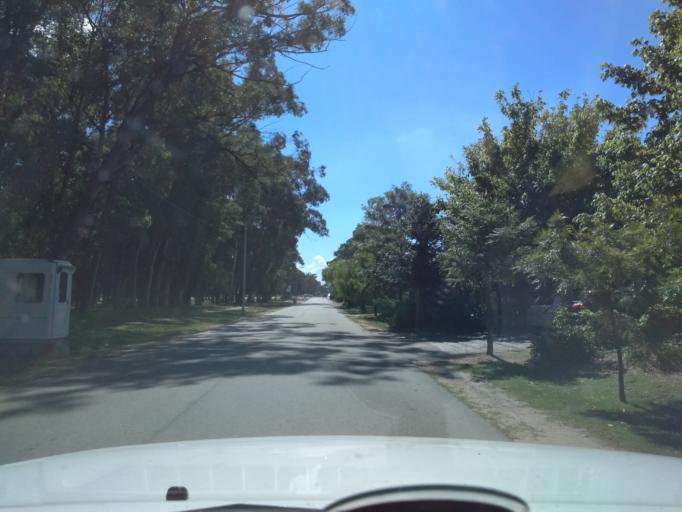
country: UY
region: Canelones
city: Barra de Carrasco
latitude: -34.8532
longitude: -56.0235
